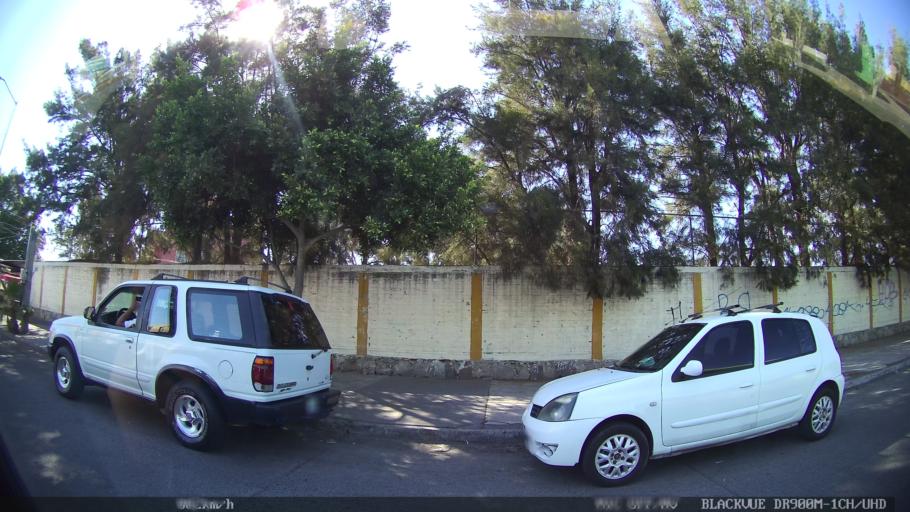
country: MX
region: Jalisco
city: Tlaquepaque
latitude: 20.6644
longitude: -103.2898
